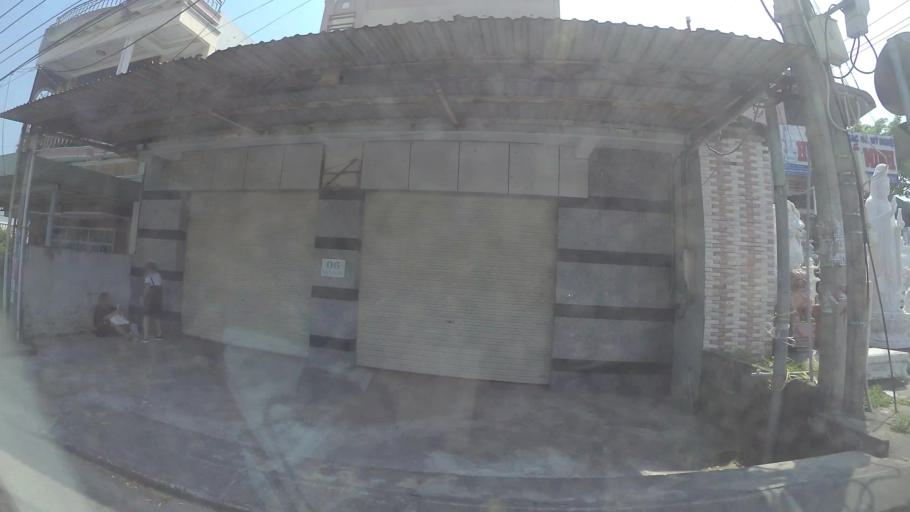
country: VN
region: Da Nang
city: Ngu Hanh Son
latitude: 16.0026
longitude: 108.2600
